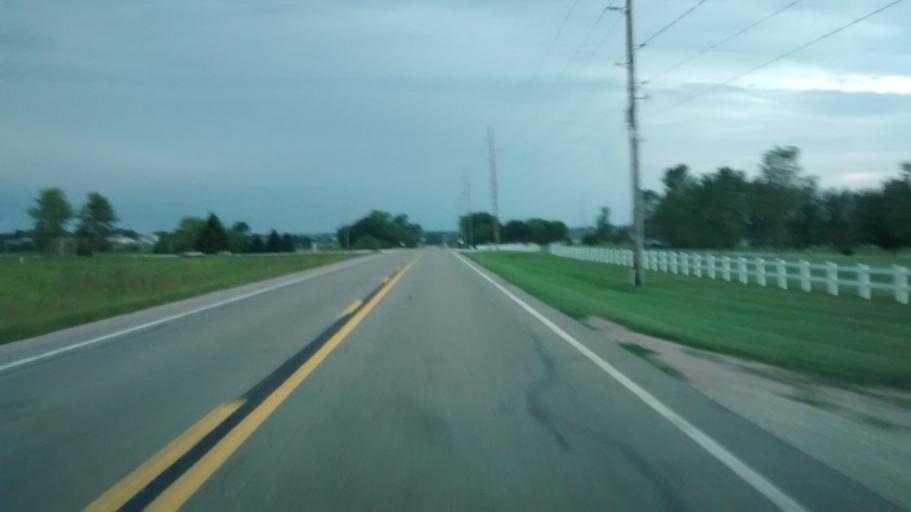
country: US
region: Iowa
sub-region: Woodbury County
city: Moville
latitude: 42.5060
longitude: -96.0615
